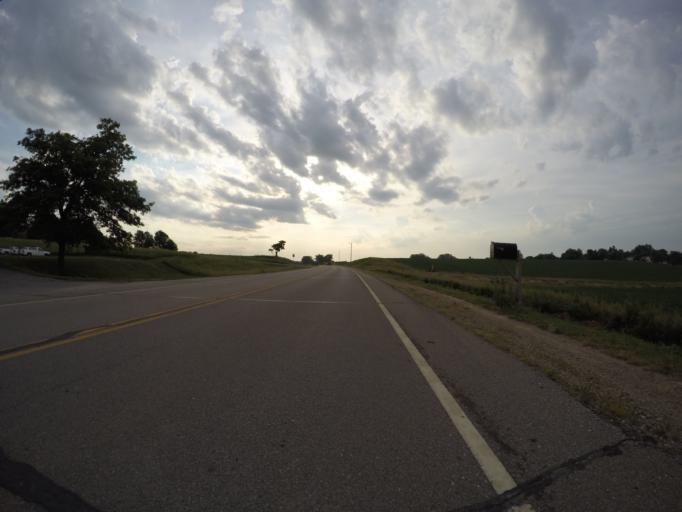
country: US
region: Kansas
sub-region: Doniphan County
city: Troy
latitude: 39.7899
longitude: -95.0838
